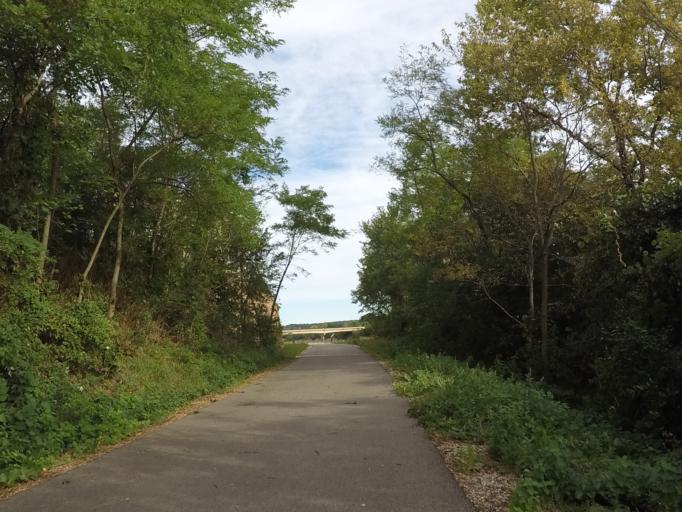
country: US
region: Wisconsin
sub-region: Sauk County
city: Prairie du Sac
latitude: 43.2891
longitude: -89.7187
